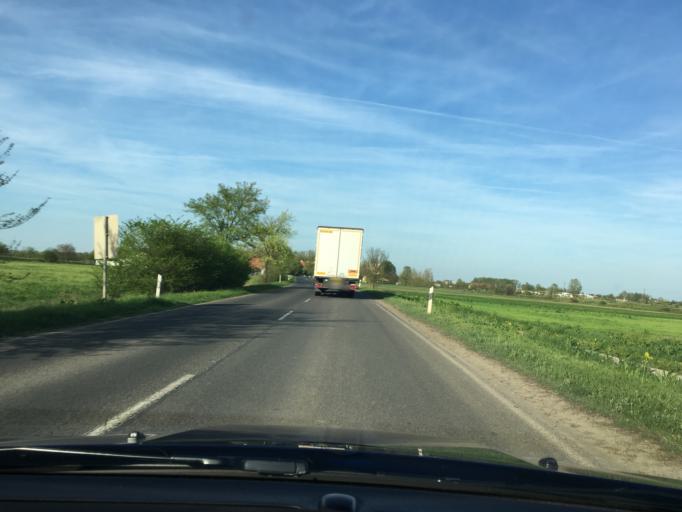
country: HU
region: Bekes
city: Szeghalom
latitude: 47.0082
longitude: 21.1312
